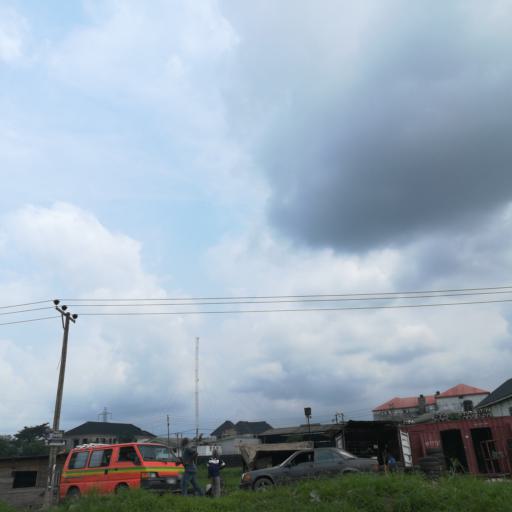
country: NG
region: Rivers
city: Port Harcourt
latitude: 4.8537
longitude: 7.0691
